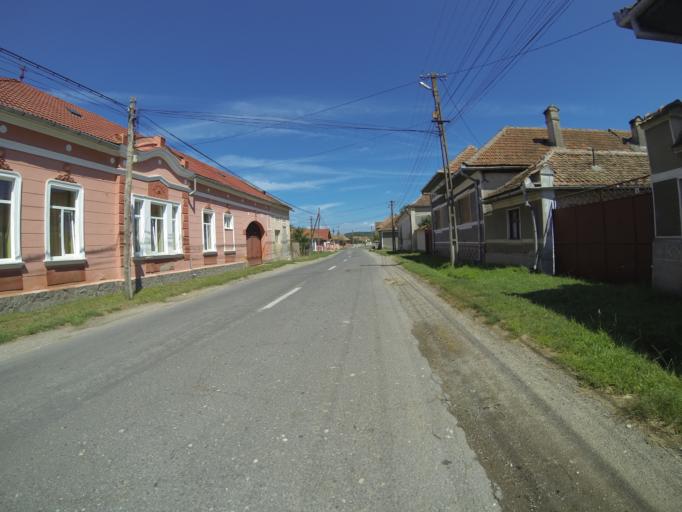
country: RO
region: Brasov
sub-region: Comuna Sinca Veche
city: Sinca Veche
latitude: 45.7630
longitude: 25.1612
